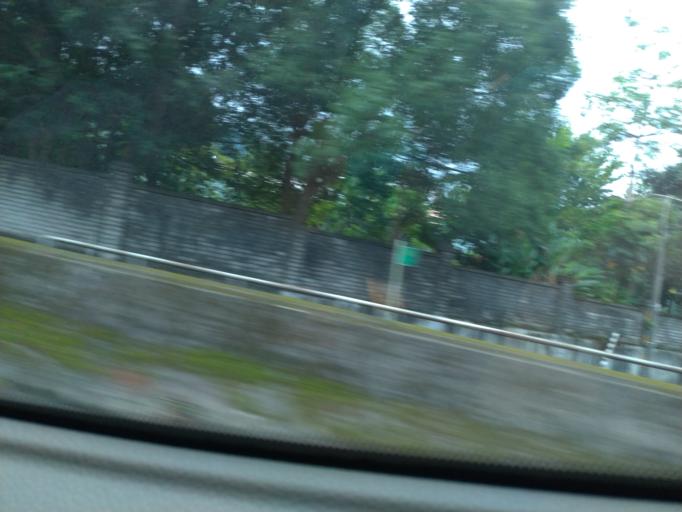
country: TW
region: Taipei
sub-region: Taipei
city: Banqiao
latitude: 24.9327
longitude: 121.4065
